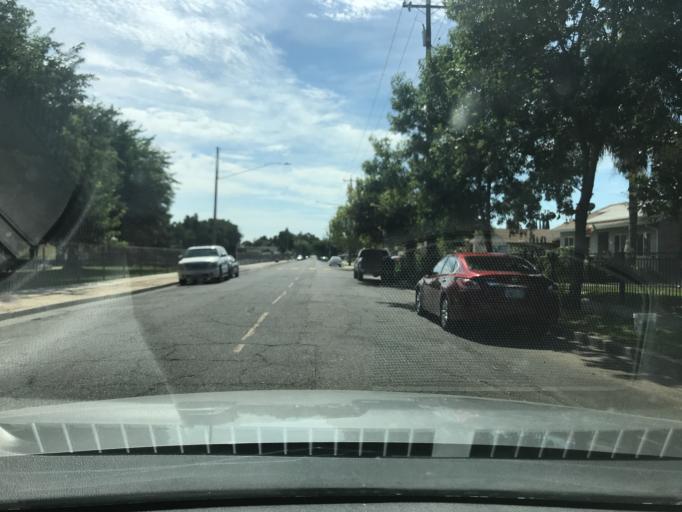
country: US
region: California
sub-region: Merced County
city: Atwater
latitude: 37.3531
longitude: -120.6128
